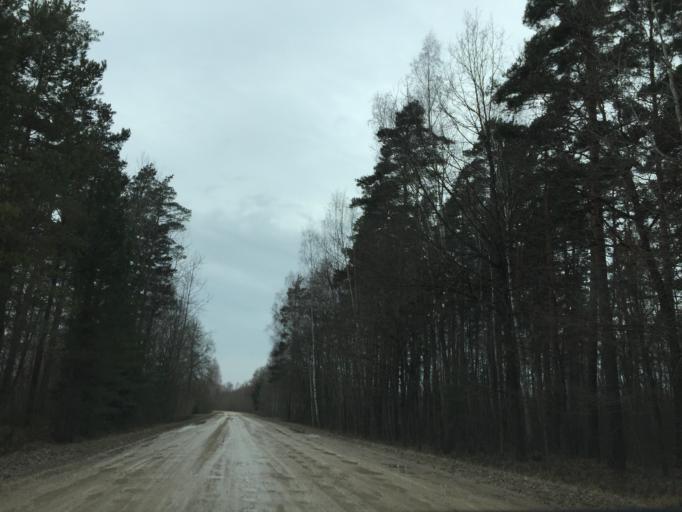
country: LV
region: Ozolnieku
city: Ozolnieki
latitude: 56.7006
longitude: 23.7359
